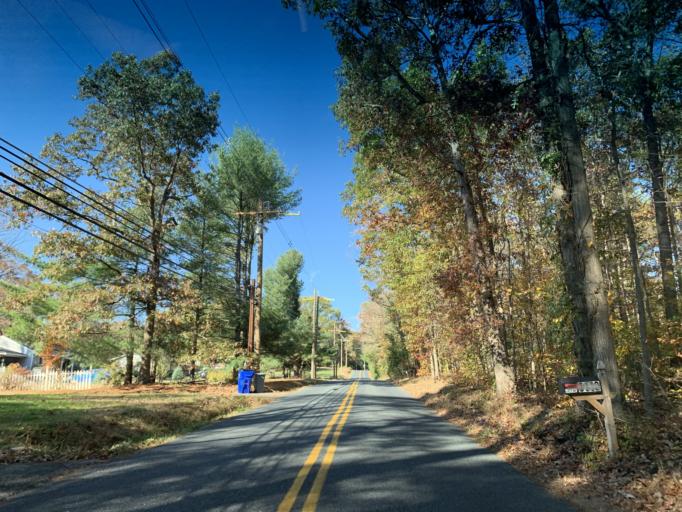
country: US
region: Maryland
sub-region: Harford County
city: Joppatowne
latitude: 39.4518
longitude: -76.3384
